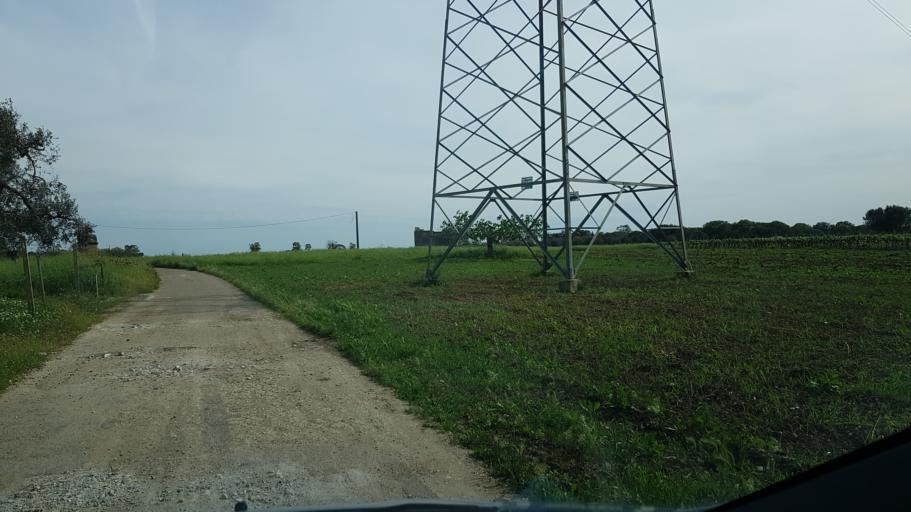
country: IT
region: Apulia
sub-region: Provincia di Brindisi
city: Tuturano
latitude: 40.5528
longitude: 17.9312
